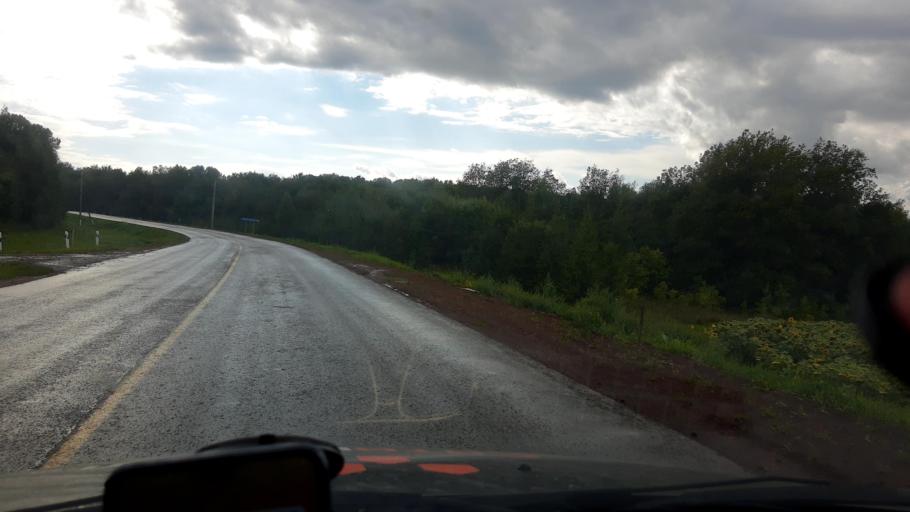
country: RU
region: Bashkortostan
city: Karmaskaly
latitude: 53.9240
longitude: 56.3550
